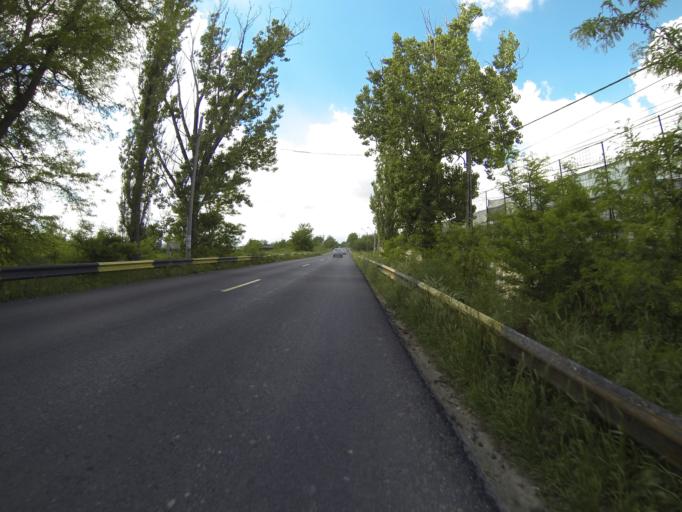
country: RO
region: Dolj
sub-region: Municipiul Craiova
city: Facai
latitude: 44.2704
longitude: 23.8213
